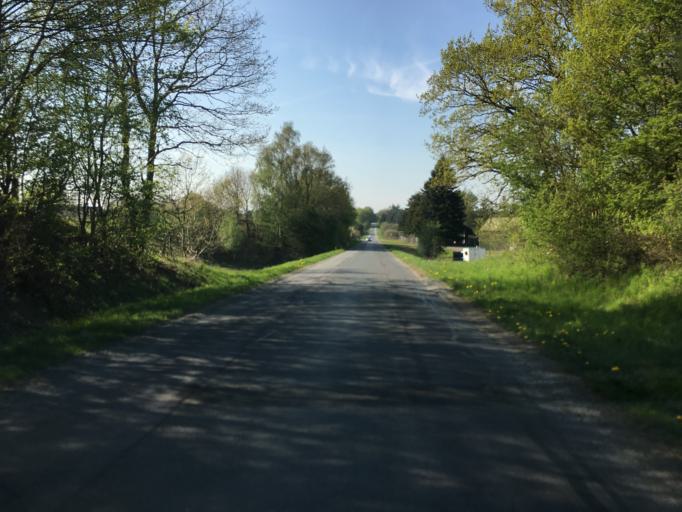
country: DK
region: South Denmark
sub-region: Haderslev Kommune
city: Vojens
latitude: 55.2353
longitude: 9.3280
